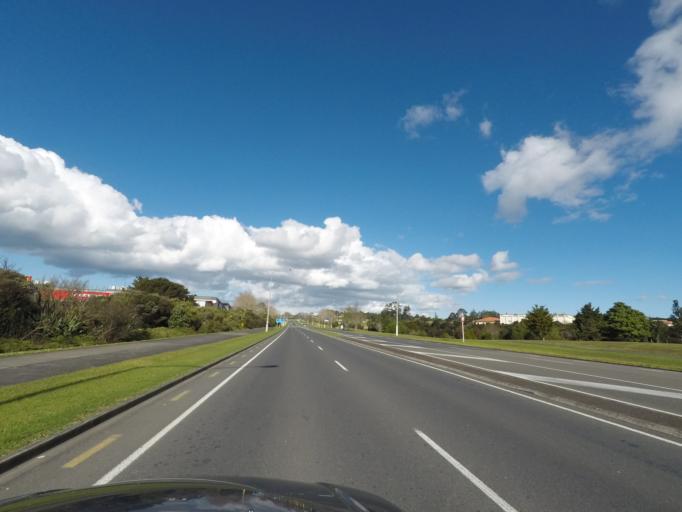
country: NZ
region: Auckland
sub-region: Auckland
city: Rothesay Bay
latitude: -36.7298
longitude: 174.7018
